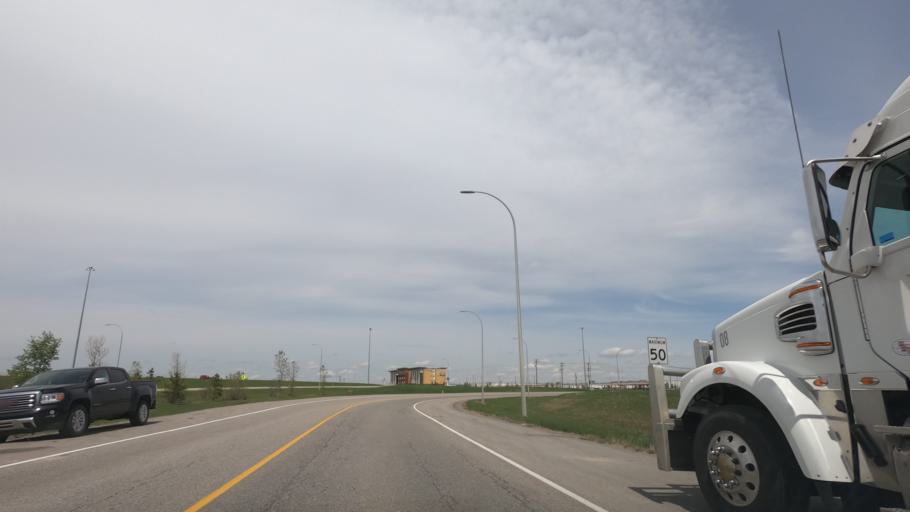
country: CA
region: Alberta
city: Airdrie
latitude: 51.2982
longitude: -113.9997
